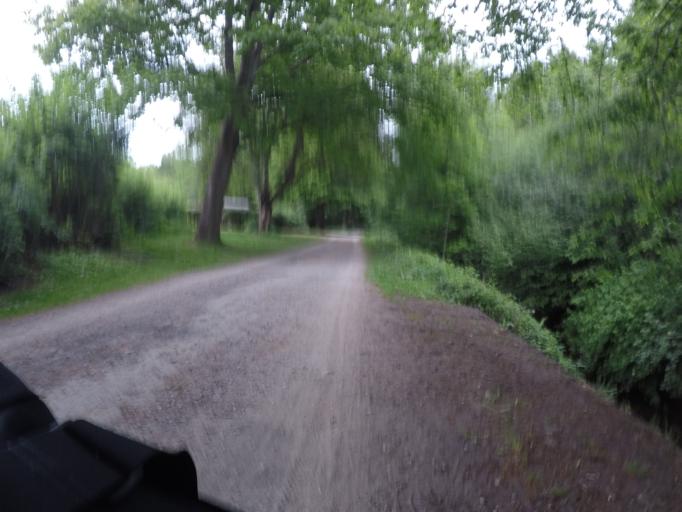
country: DE
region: Hamburg
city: Fuhlsbuettel
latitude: 53.6322
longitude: 9.9807
